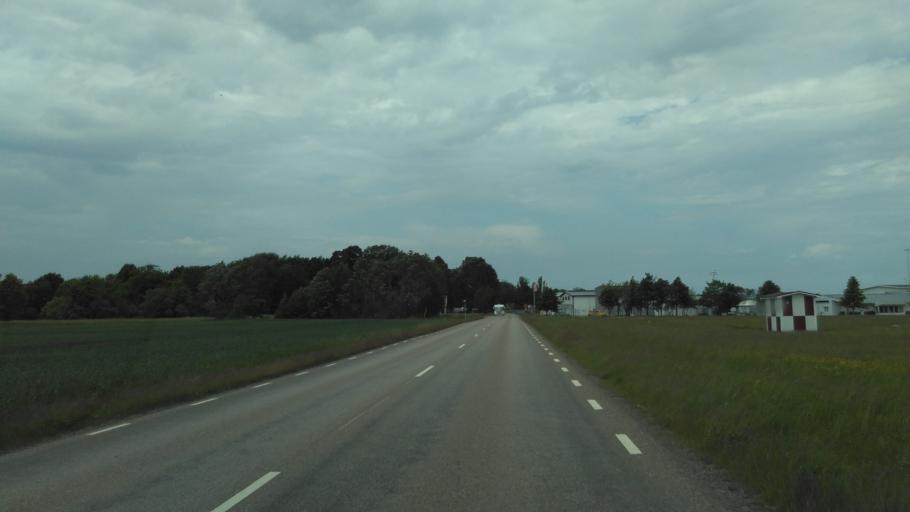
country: SE
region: Vaestra Goetaland
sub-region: Lidkopings Kommun
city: Lidkoping
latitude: 58.4599
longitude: 13.1548
